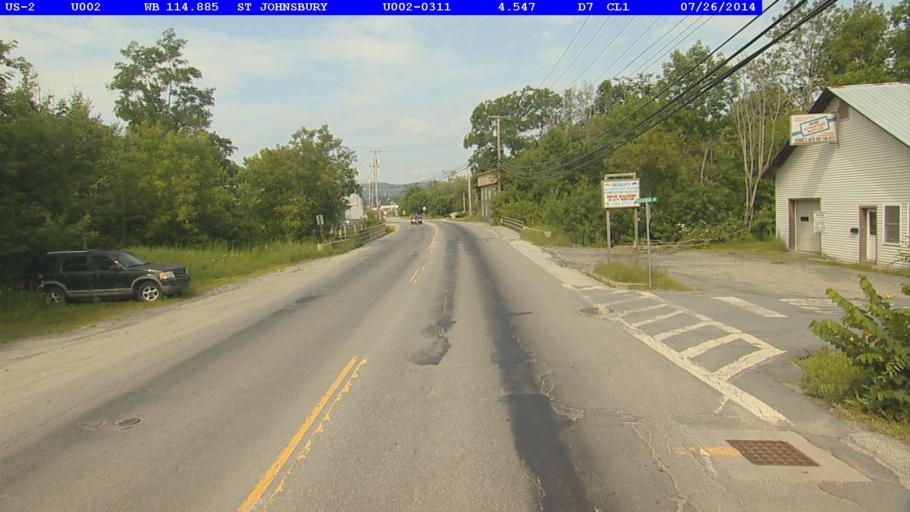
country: US
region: Vermont
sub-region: Caledonia County
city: Saint Johnsbury
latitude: 44.4217
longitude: -71.9972
